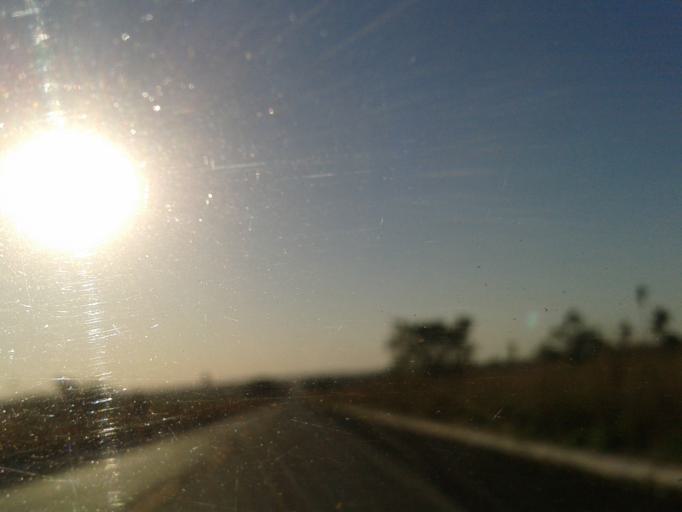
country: BR
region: Minas Gerais
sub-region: Santa Vitoria
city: Santa Vitoria
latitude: -19.0888
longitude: -50.3480
